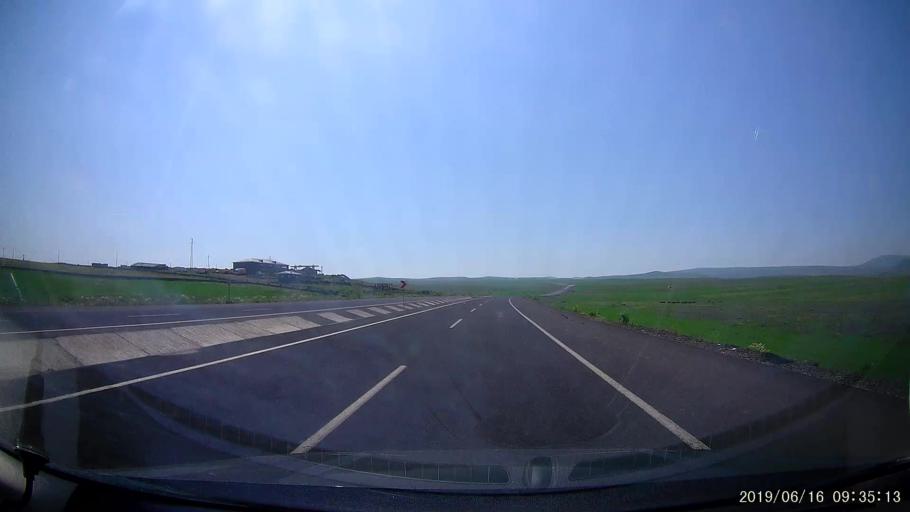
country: TR
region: Kars
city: Kars
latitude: 40.5751
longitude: 43.1522
